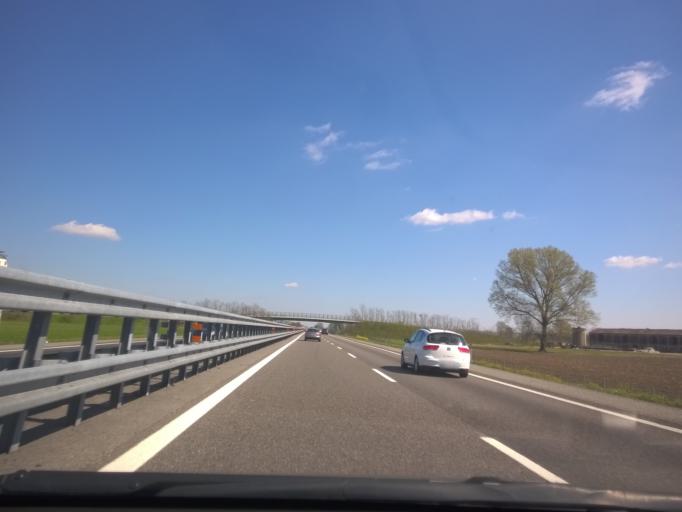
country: IT
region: Emilia-Romagna
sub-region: Provincia di Piacenza
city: Sarmato
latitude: 45.0706
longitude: 9.4926
